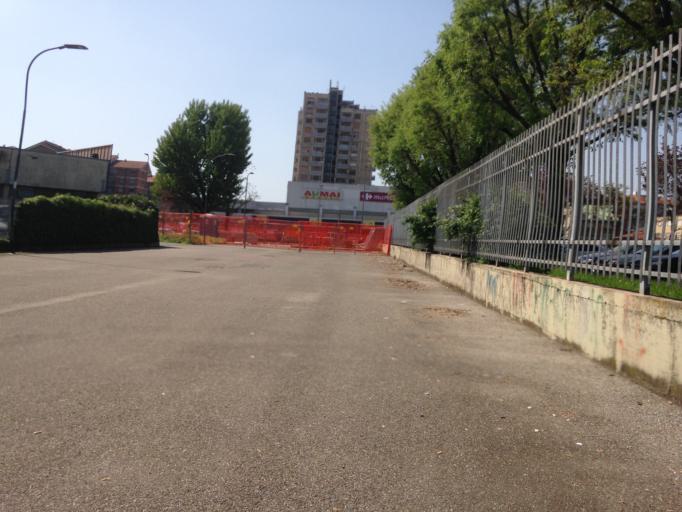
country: IT
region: Lombardy
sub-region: Citta metropolitana di Milano
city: Milano
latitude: 45.4273
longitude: 9.1794
